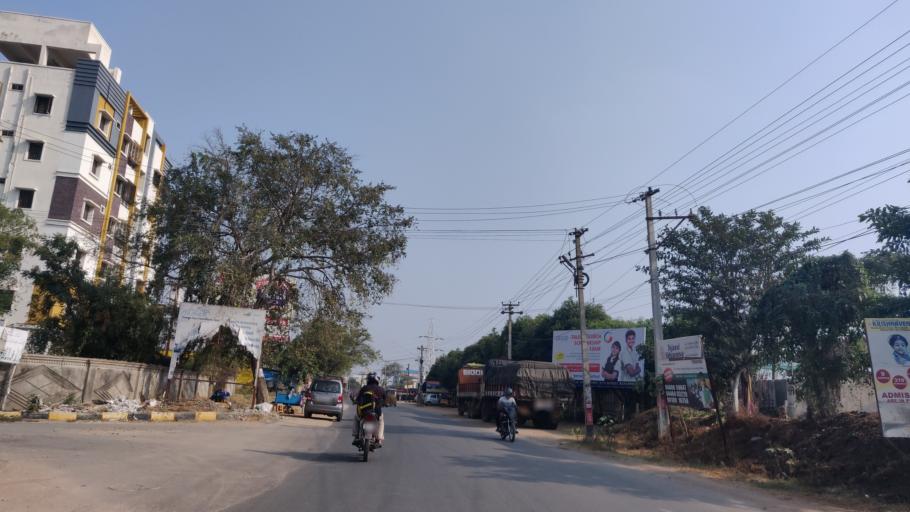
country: IN
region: Telangana
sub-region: Rangareddi
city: Uppal Kalan
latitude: 17.3978
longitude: 78.5875
